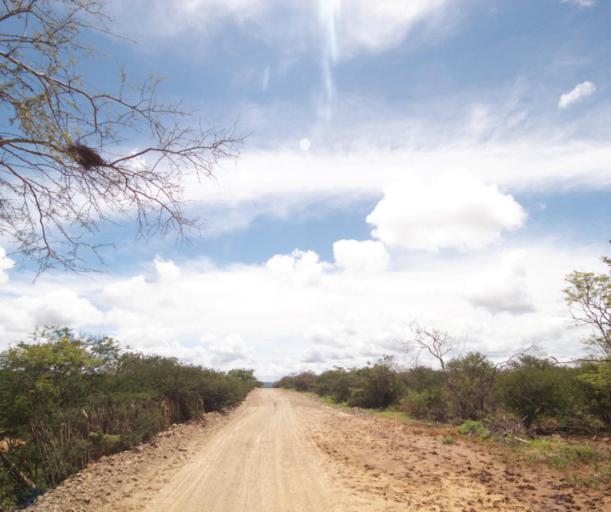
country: BR
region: Bahia
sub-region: Tanhacu
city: Tanhacu
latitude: -14.1923
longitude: -41.0455
